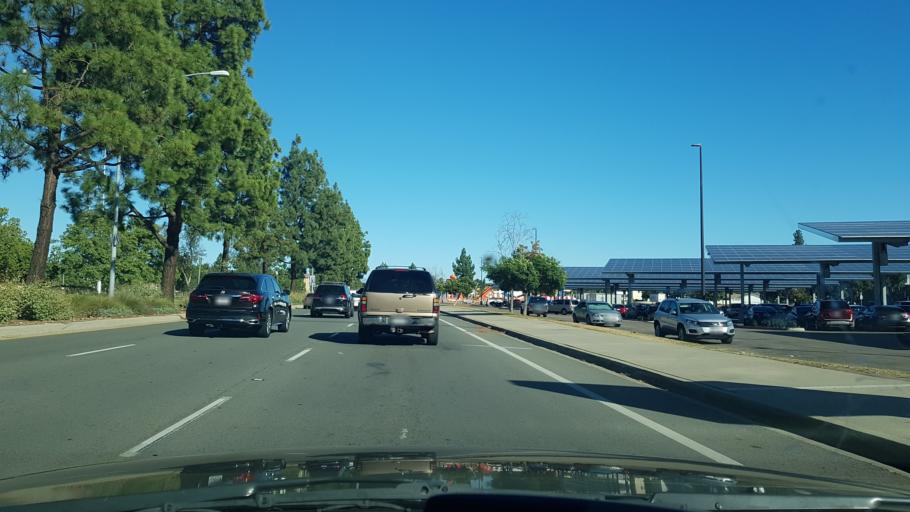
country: US
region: California
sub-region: San Diego County
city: Fairbanks Ranch
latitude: 32.9127
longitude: -117.1416
